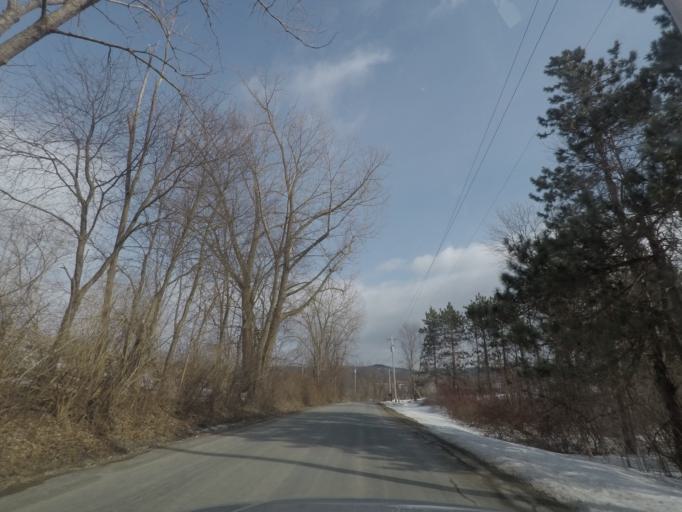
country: US
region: New York
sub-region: Rensselaer County
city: Poestenkill
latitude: 42.7846
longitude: -73.5624
